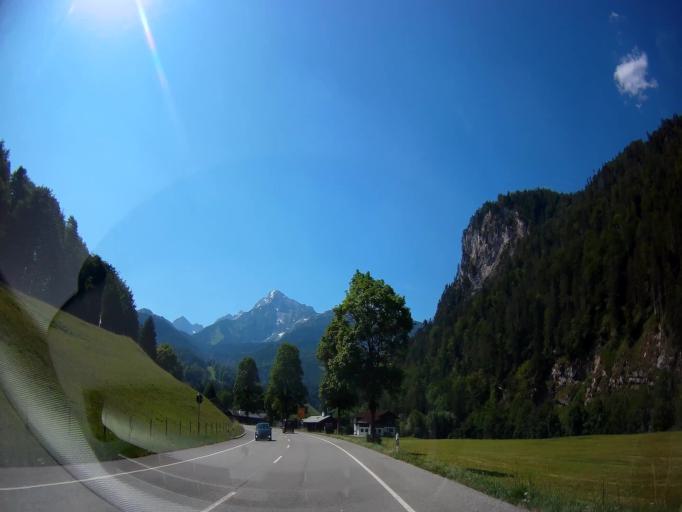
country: DE
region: Bavaria
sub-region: Upper Bavaria
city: Marktschellenberg
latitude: 47.6595
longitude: 13.0374
